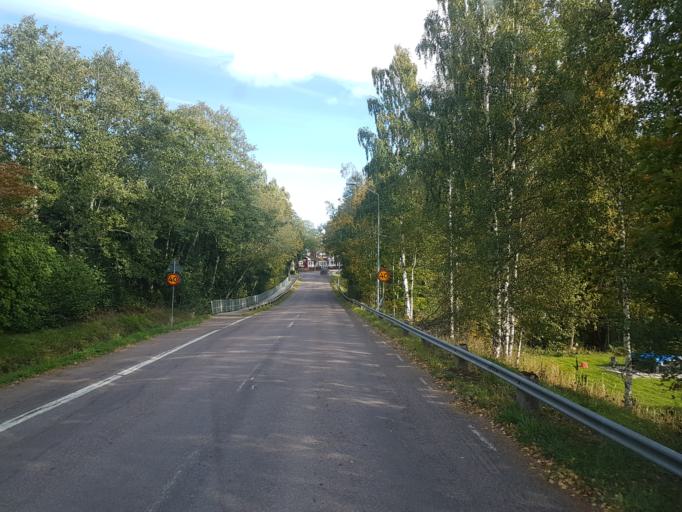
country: SE
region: Dalarna
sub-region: Borlange Kommun
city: Ornas
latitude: 60.4138
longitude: 15.6066
